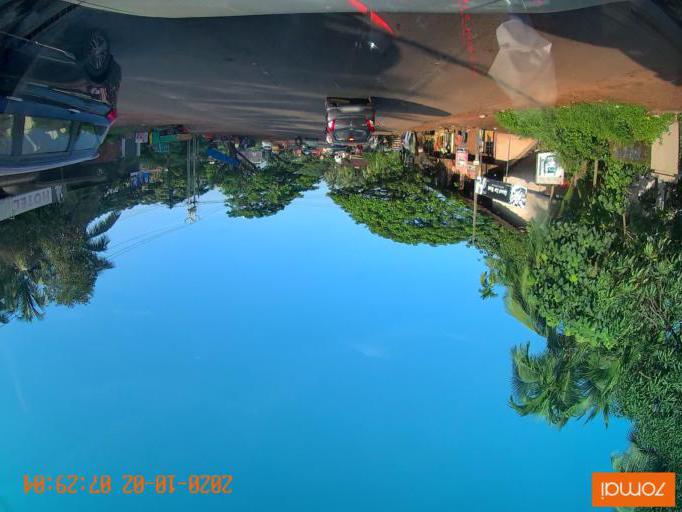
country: IN
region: Kerala
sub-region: Malappuram
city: Pariyapuram
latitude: 11.0321
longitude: 75.9403
